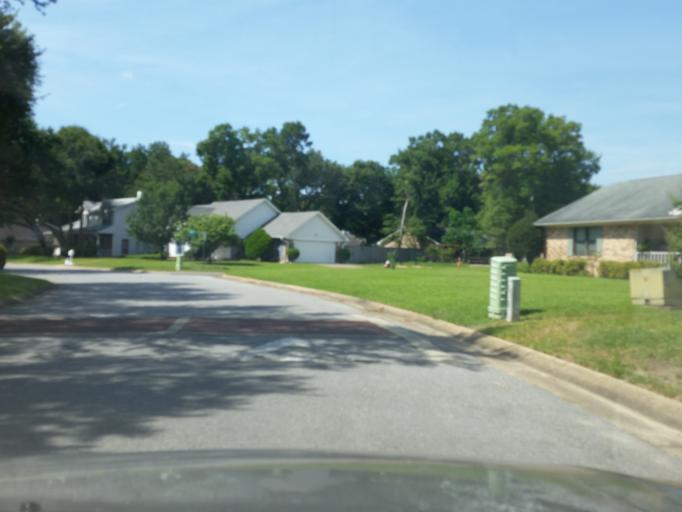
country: US
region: Florida
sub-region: Escambia County
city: Ferry Pass
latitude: 30.5208
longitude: -87.2065
